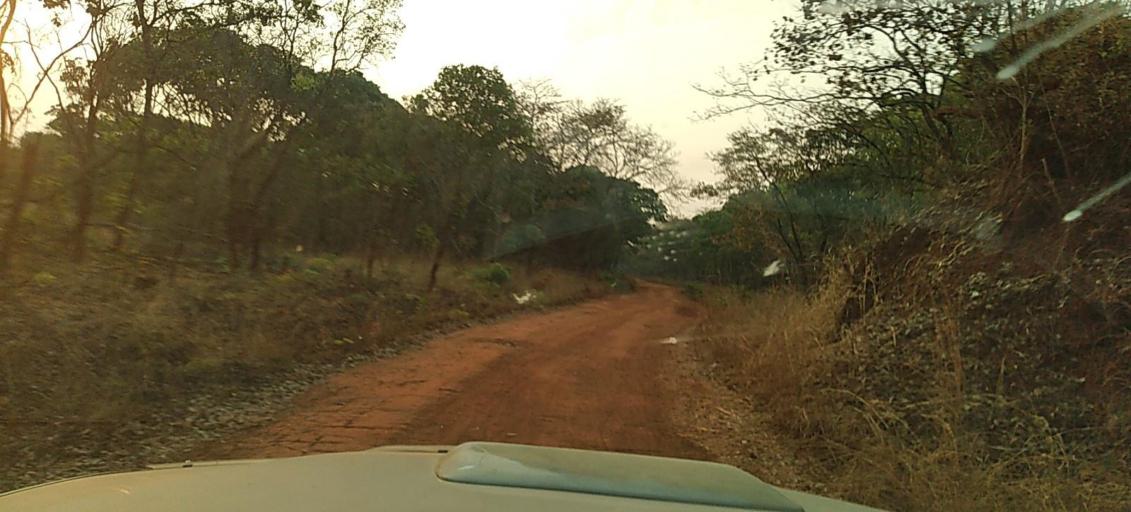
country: ZM
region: North-Western
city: Kasempa
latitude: -13.0791
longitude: 26.3925
